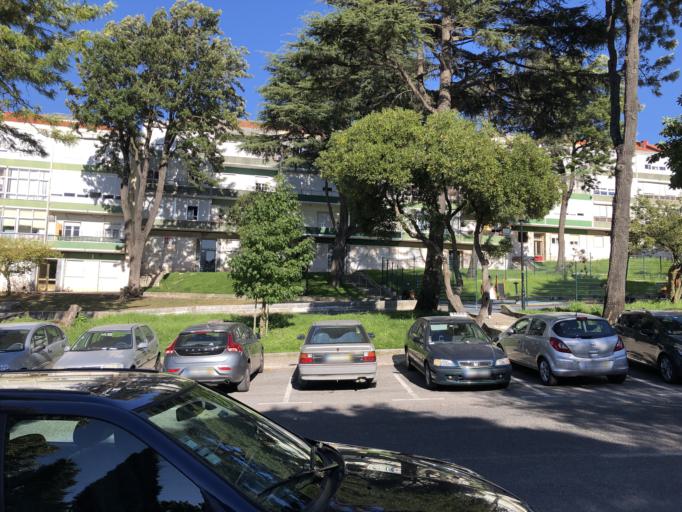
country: PT
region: Lisbon
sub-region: Sintra
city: Queluz
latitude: 38.7576
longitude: -9.2434
